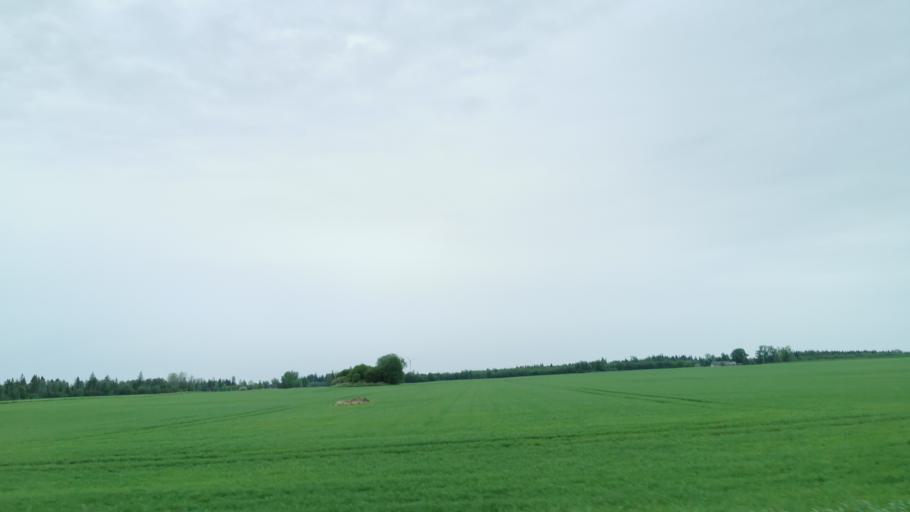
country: EE
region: Laeaene-Virumaa
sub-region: Vaeike-Maarja vald
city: Vaike-Maarja
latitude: 59.1614
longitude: 26.2894
